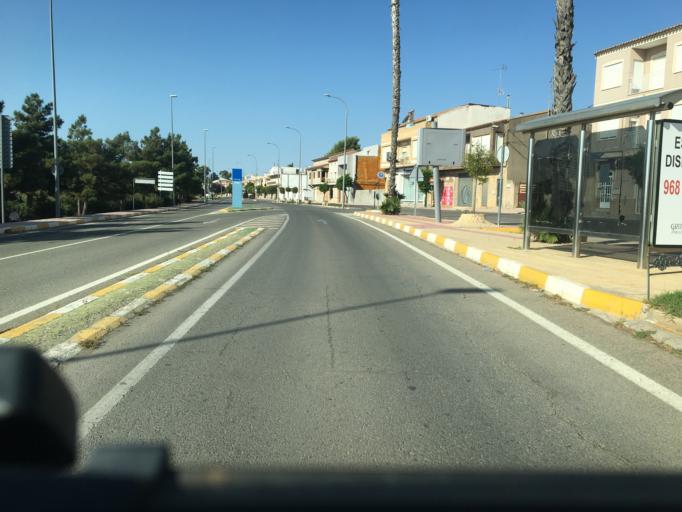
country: ES
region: Murcia
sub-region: Murcia
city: Puerto Lumbreras
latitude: 37.5515
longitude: -1.8141
